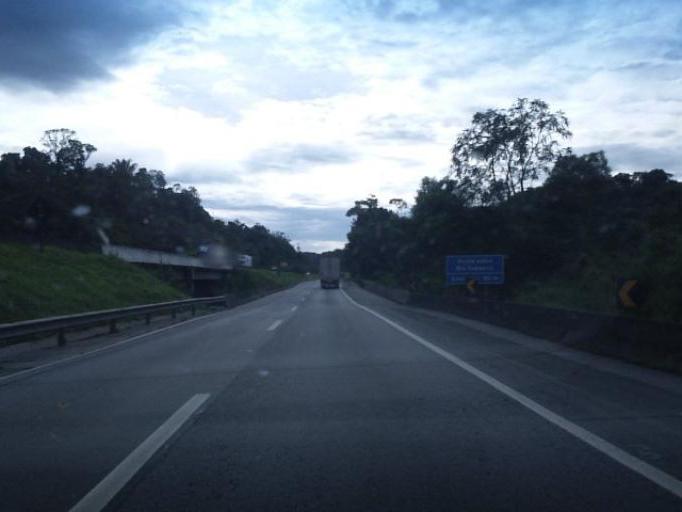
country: BR
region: Parana
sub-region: Antonina
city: Antonina
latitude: -25.0983
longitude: -48.6818
